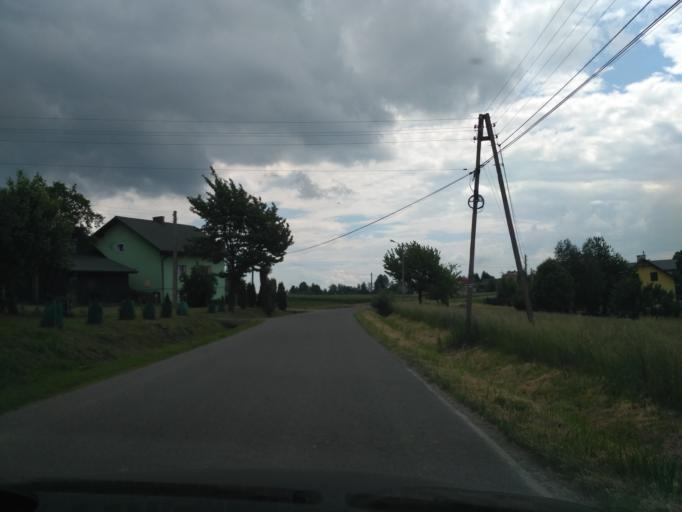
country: PL
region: Subcarpathian Voivodeship
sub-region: Powiat rzeszowski
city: Hyzne
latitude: 49.9340
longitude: 22.1820
